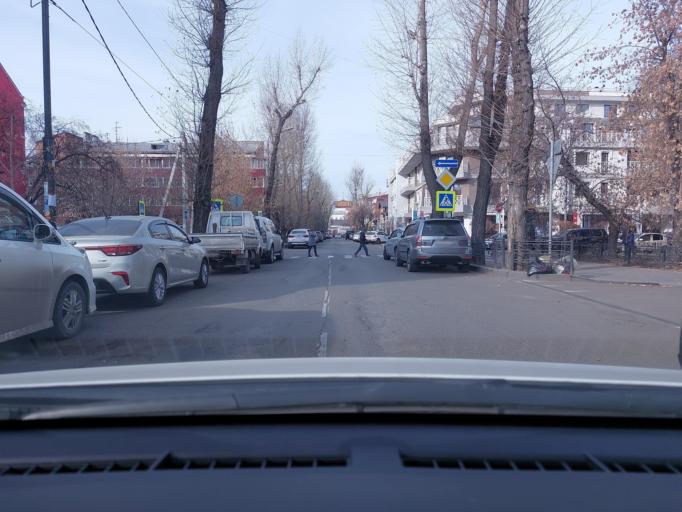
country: RU
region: Irkutsk
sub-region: Irkutskiy Rayon
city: Irkutsk
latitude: 52.2819
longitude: 104.2893
